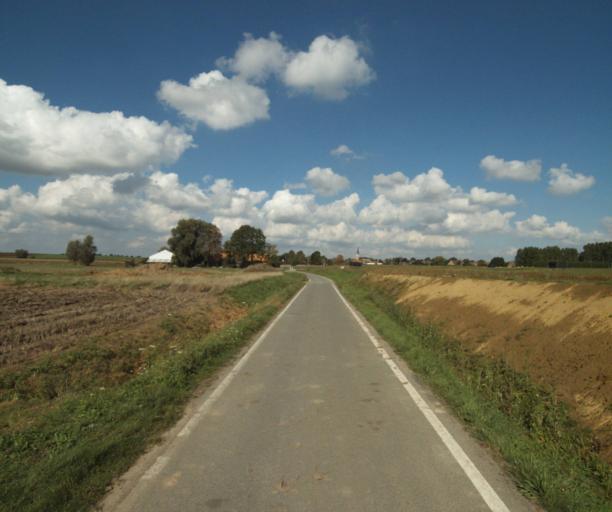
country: FR
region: Nord-Pas-de-Calais
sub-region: Departement du Nord
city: Herlies
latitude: 50.5696
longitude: 2.8485
